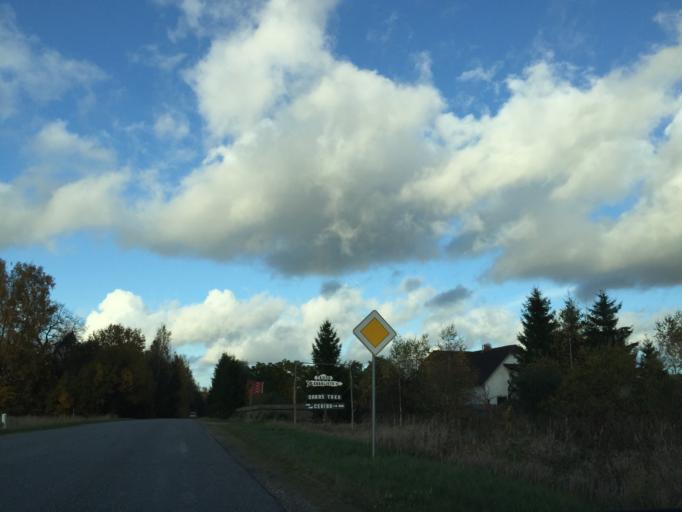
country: LV
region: Ogre
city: Jumprava
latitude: 56.7758
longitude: 25.0052
